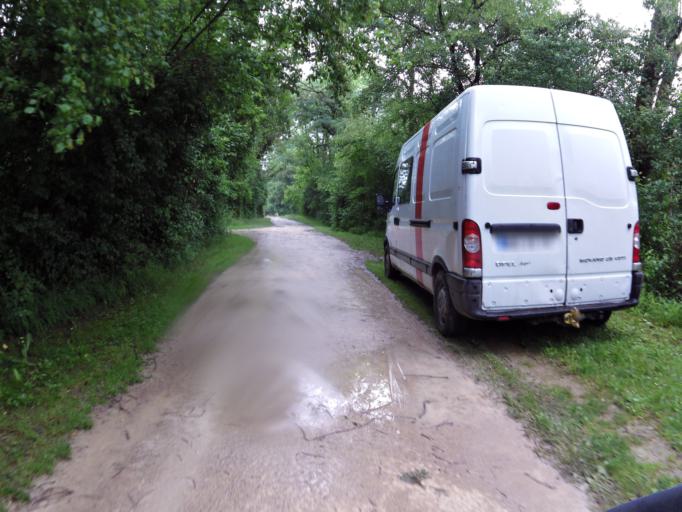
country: FR
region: Poitou-Charentes
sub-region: Departement de la Charente
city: Gond-Pontouvre
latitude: 45.6718
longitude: 0.1546
